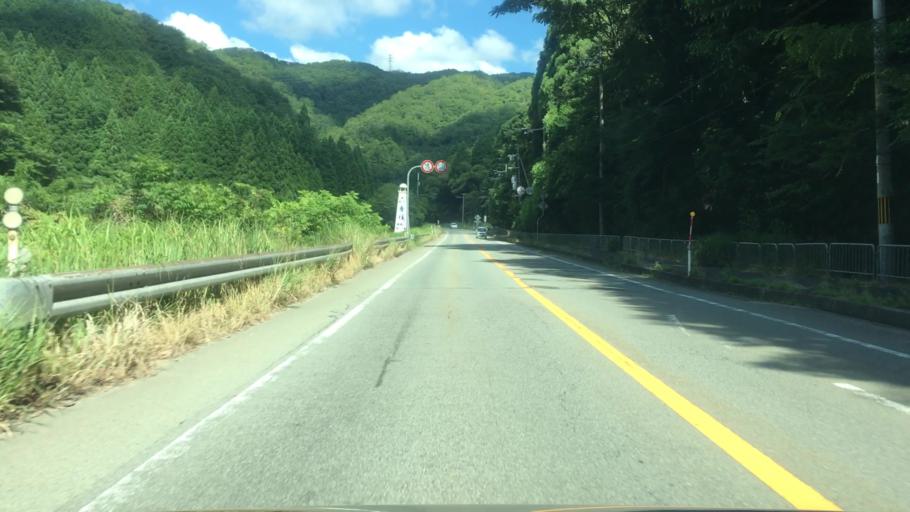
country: JP
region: Hyogo
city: Toyooka
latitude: 35.5765
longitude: 134.7549
